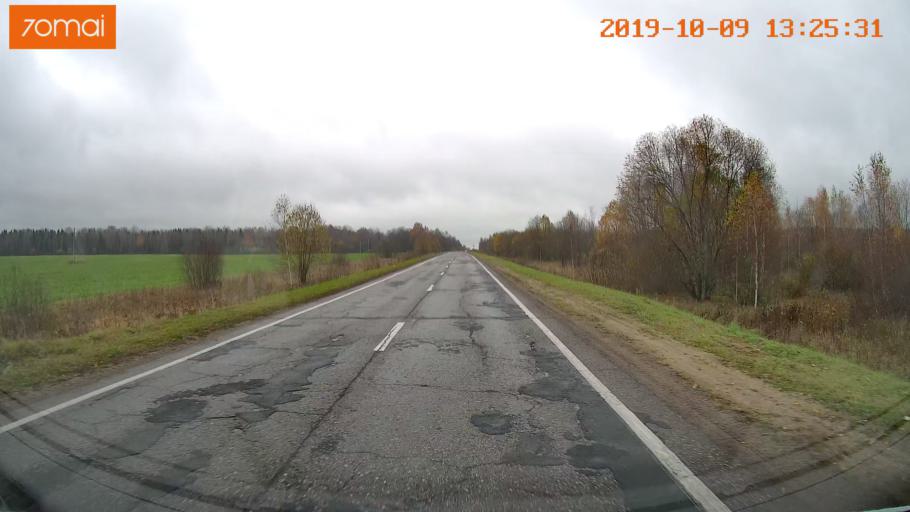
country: RU
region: Jaroslavl
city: Lyubim
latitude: 58.3277
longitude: 40.9120
